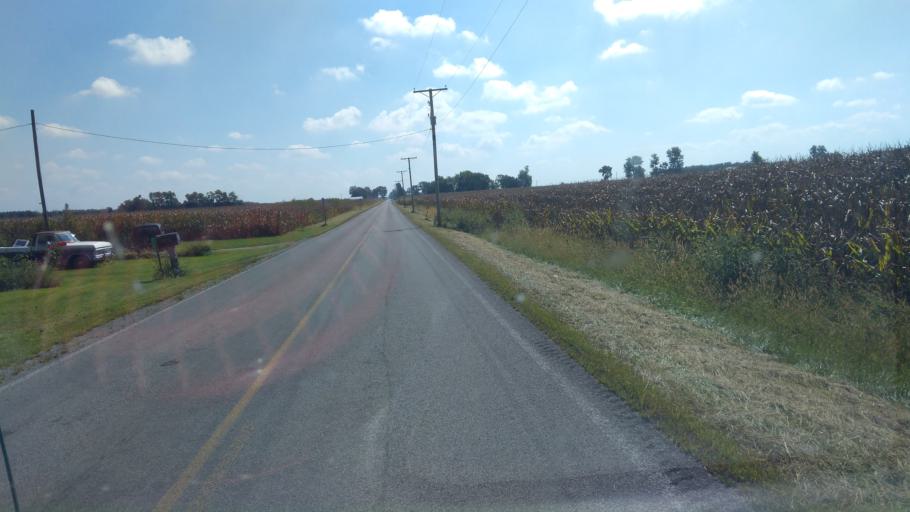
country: US
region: Ohio
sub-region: Hardin County
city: Ada
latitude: 40.7741
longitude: -83.7849
